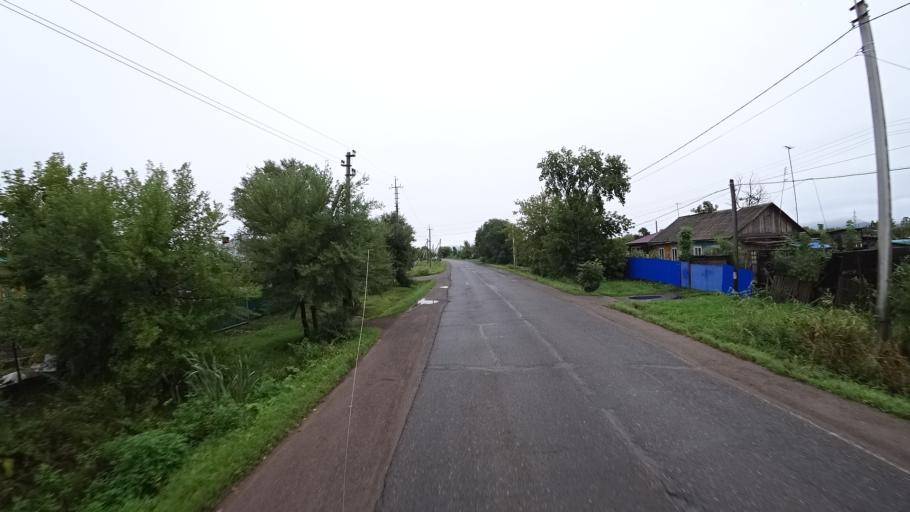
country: RU
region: Primorskiy
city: Monastyrishche
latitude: 44.1988
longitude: 132.4635
